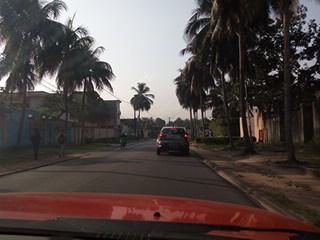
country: CI
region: Lagunes
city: Abobo
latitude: 5.3707
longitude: -3.9911
